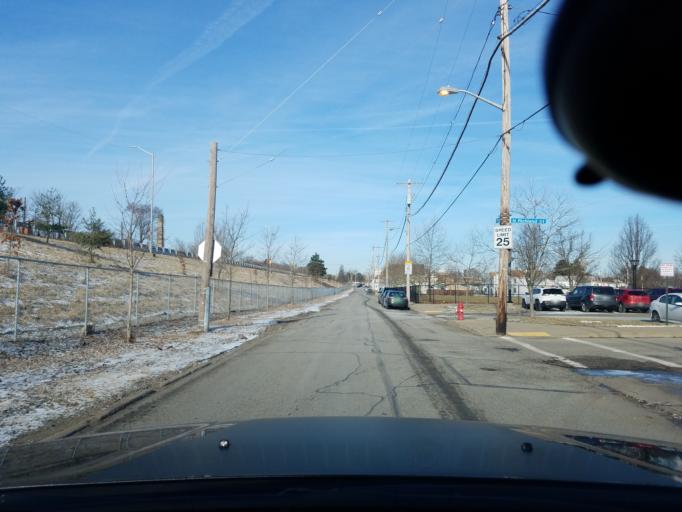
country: US
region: Pennsylvania
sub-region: Allegheny County
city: Wilkinsburg
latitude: 40.4512
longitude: -79.8939
